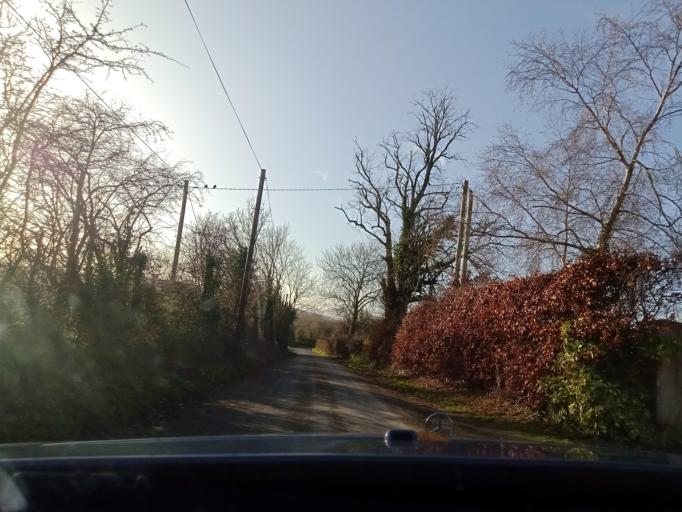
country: IE
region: Leinster
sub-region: Kilkenny
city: Callan
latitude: 52.4876
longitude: -7.4017
